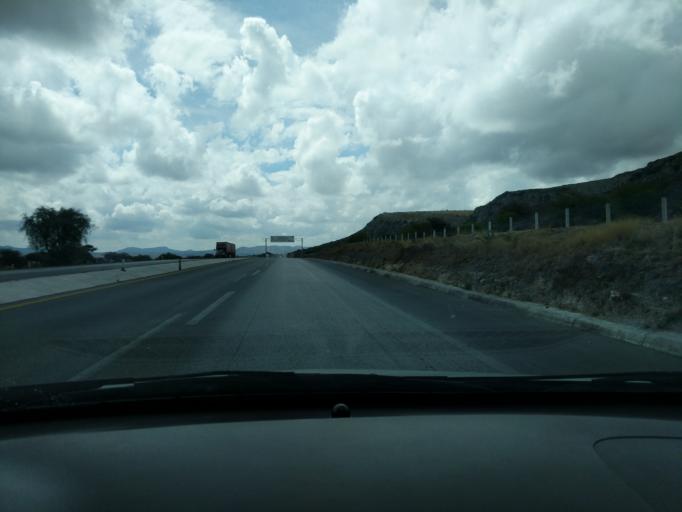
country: MX
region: Zacatecas
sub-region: Pinos
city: Santiago
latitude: 22.4004
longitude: -101.3744
